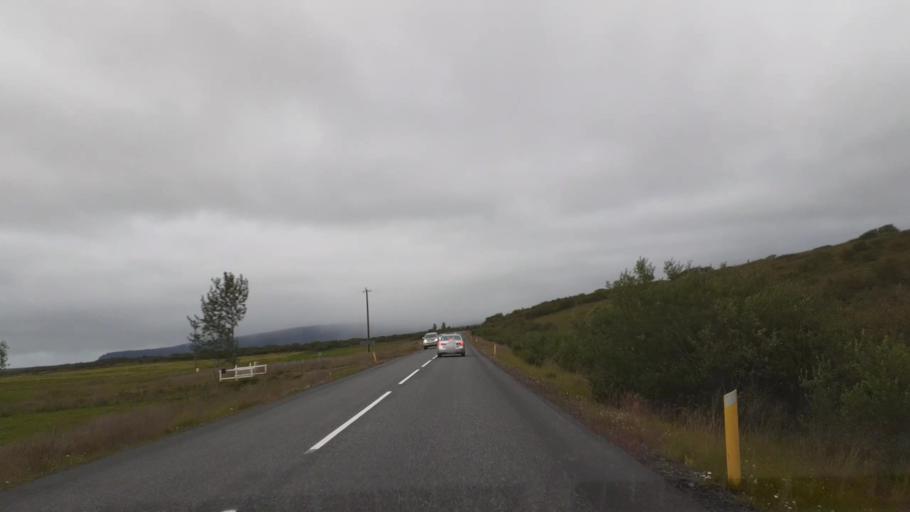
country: IS
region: Northeast
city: Husavik
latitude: 66.0671
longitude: -16.4411
